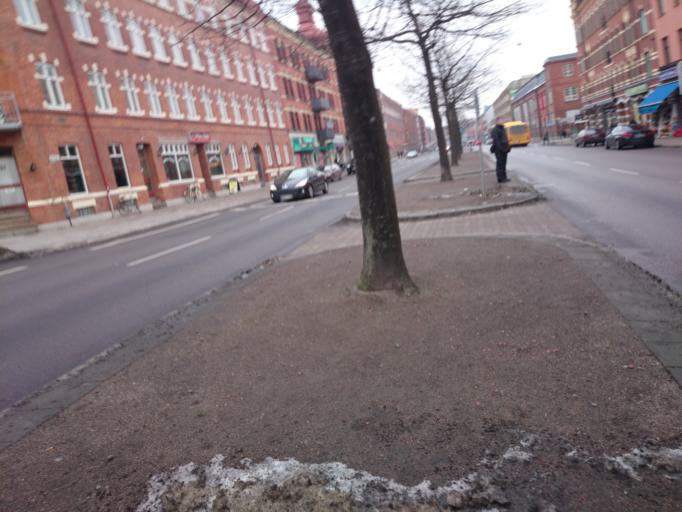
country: SE
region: Skane
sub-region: Malmo
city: Malmoe
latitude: 55.5925
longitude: 13.0075
